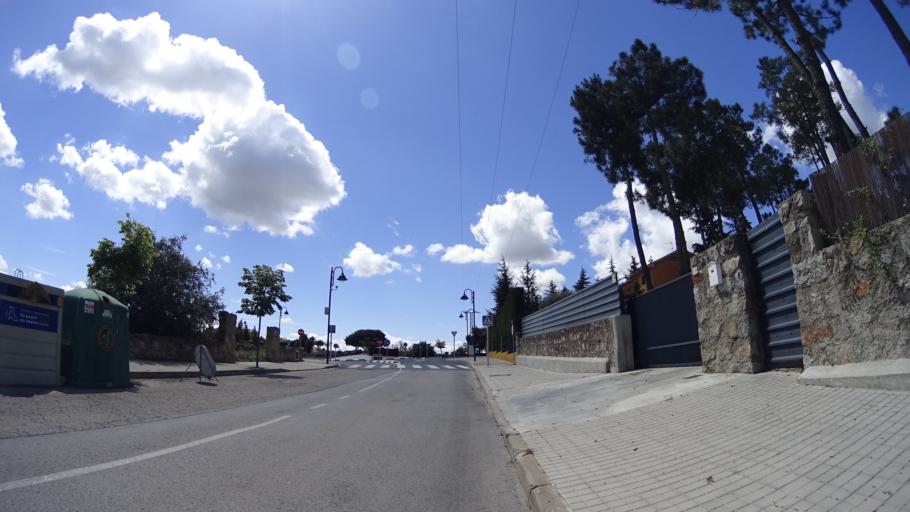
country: ES
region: Madrid
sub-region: Provincia de Madrid
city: Galapagar
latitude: 40.5707
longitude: -4.0078
